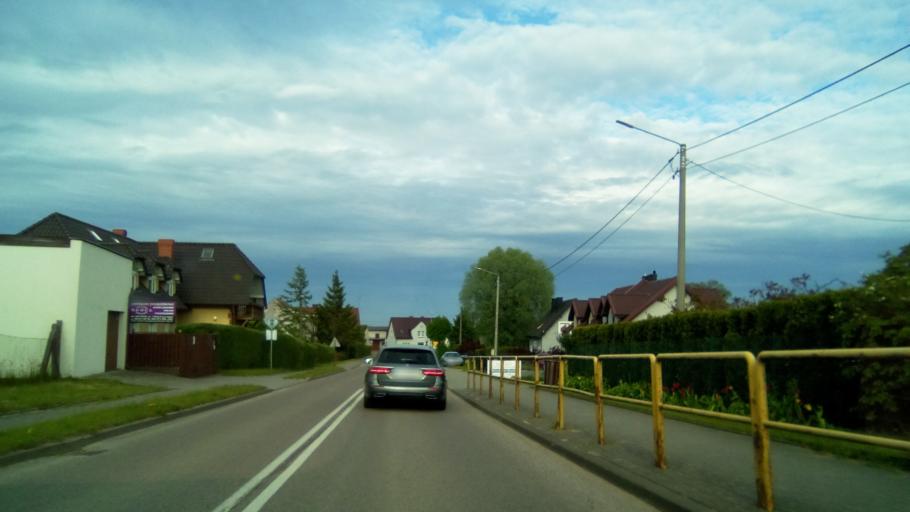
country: PL
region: Pomeranian Voivodeship
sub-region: Powiat pucki
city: Gniezdzewo
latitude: 54.7464
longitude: 18.3769
